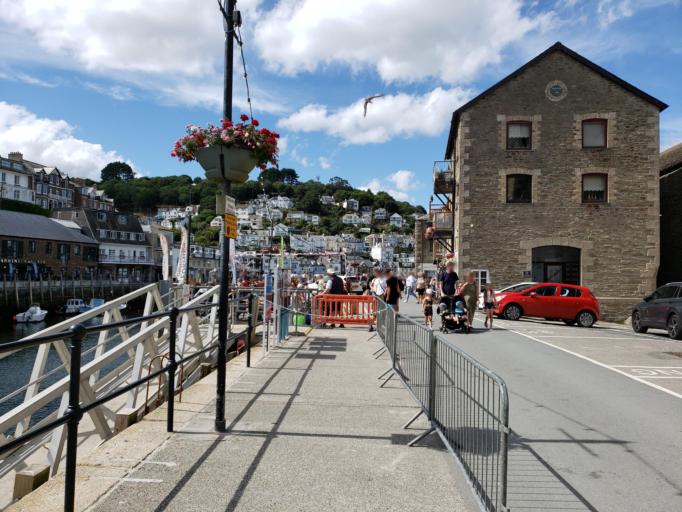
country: GB
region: England
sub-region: Cornwall
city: Looe
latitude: 50.3522
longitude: -4.4536
